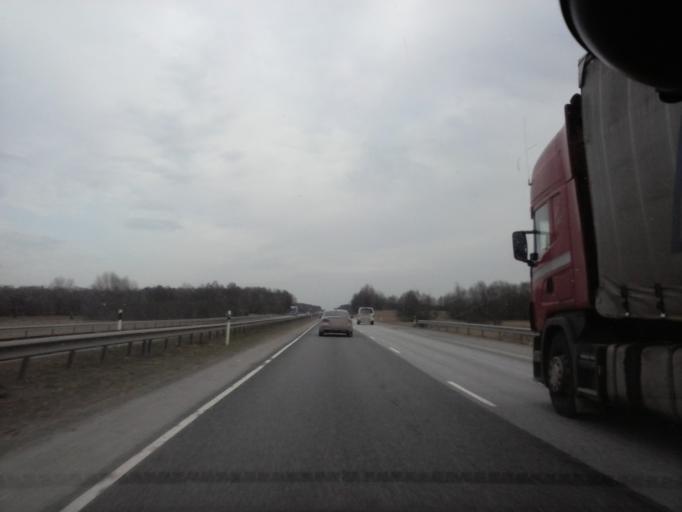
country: EE
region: Harju
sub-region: Rae vald
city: Jueri
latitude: 59.3369
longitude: 24.9059
